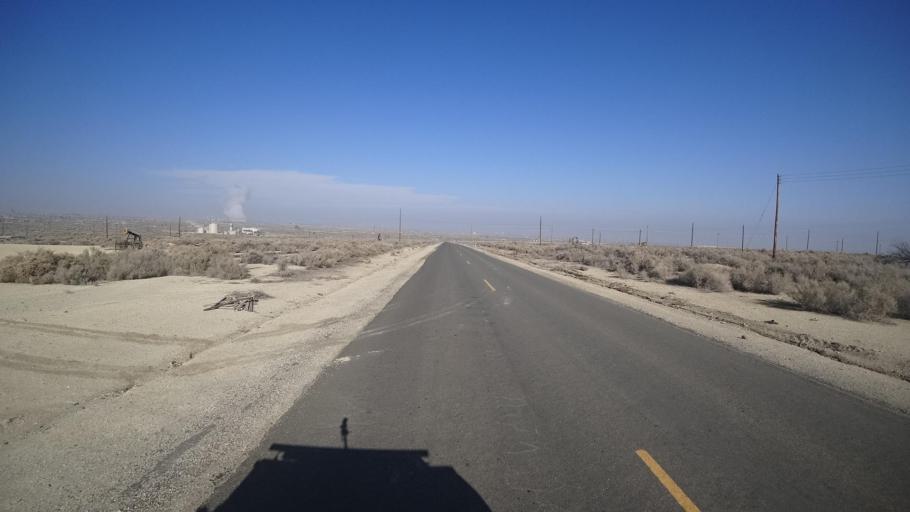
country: US
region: California
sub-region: Kern County
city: Taft Heights
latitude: 35.1899
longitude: -119.5675
